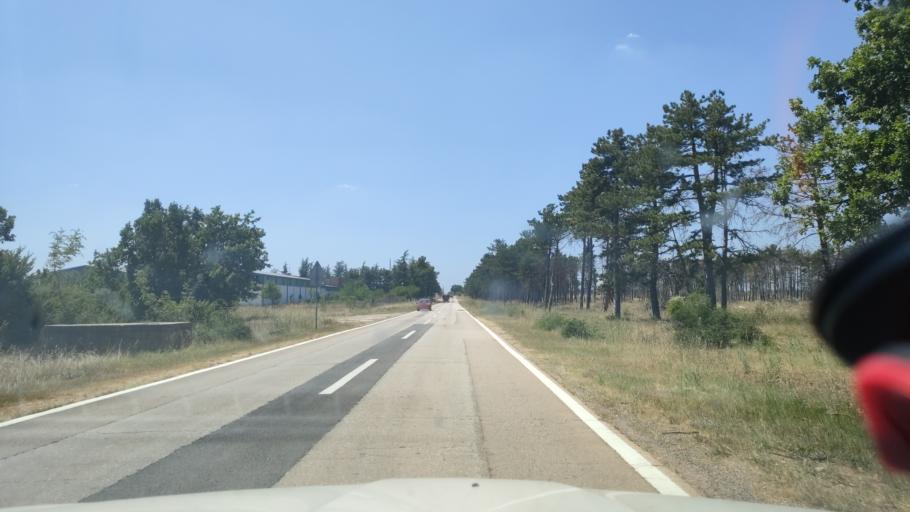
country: HR
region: Sibensko-Kniniska
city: Kistanje
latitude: 43.9893
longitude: 15.9766
